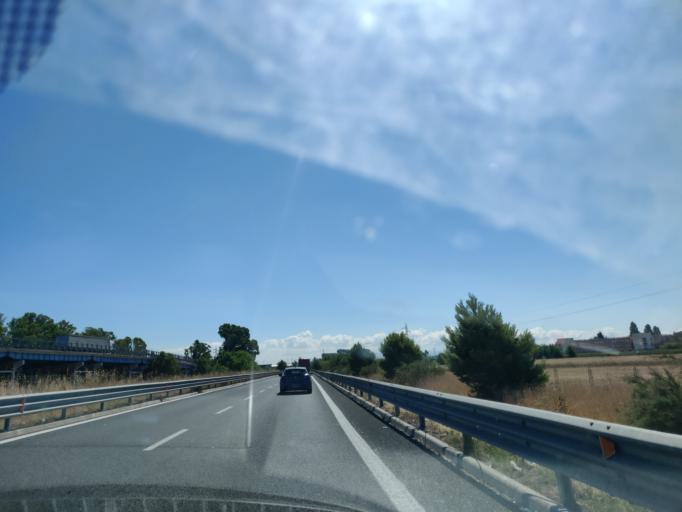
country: IT
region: Latium
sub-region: Citta metropolitana di Roma Capitale
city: Npp 23 (Parco Leonardo)
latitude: 41.8090
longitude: 12.3095
